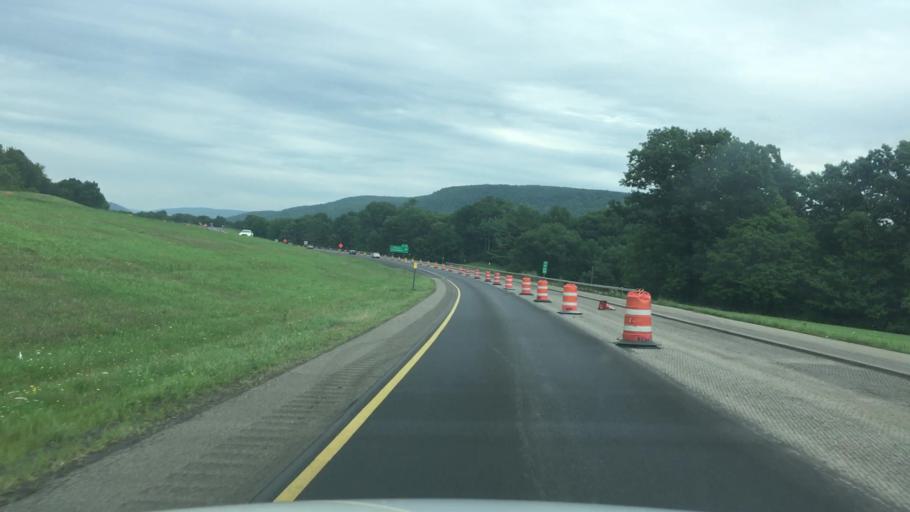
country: US
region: New York
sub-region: Otsego County
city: Oneonta
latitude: 42.4566
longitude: -75.0187
